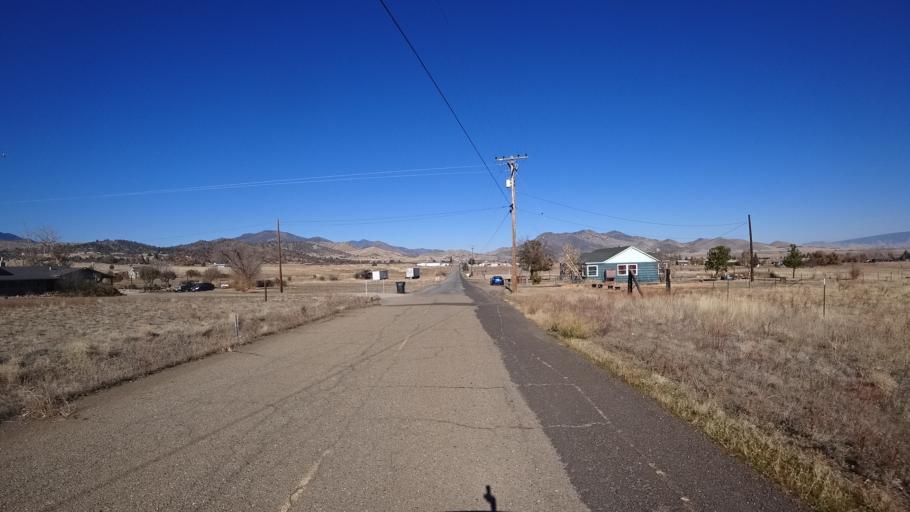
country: US
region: California
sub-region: Siskiyou County
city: Yreka
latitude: 41.7369
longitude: -122.5932
